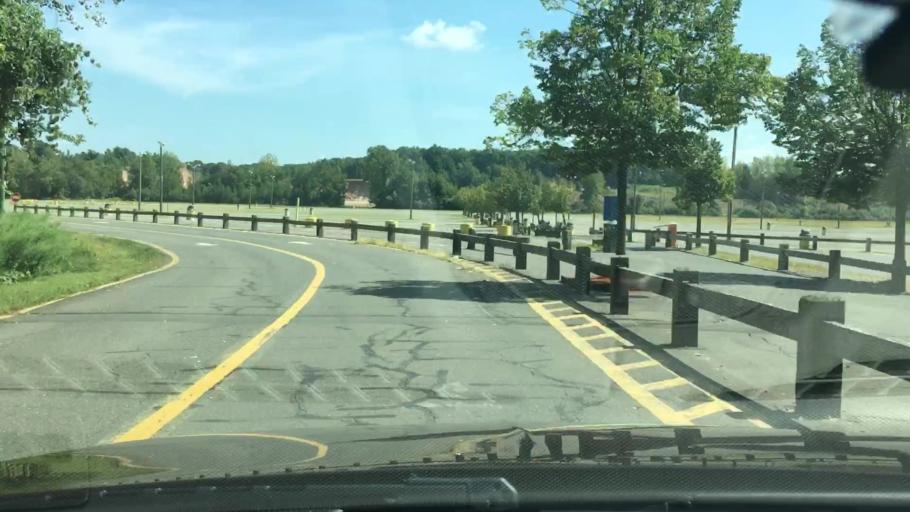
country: US
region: Connecticut
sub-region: Hartford County
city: Bristol
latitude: 41.6414
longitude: -72.9206
